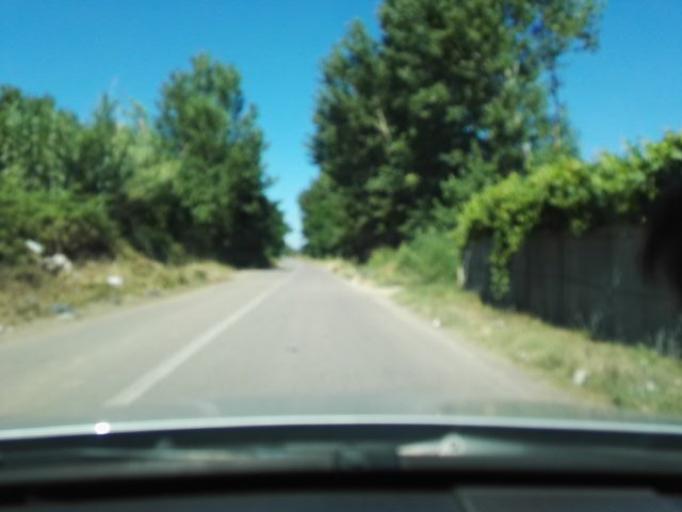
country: IT
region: Campania
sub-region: Provincia di Caserta
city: Villa di Briano
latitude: 40.9854
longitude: 14.1535
